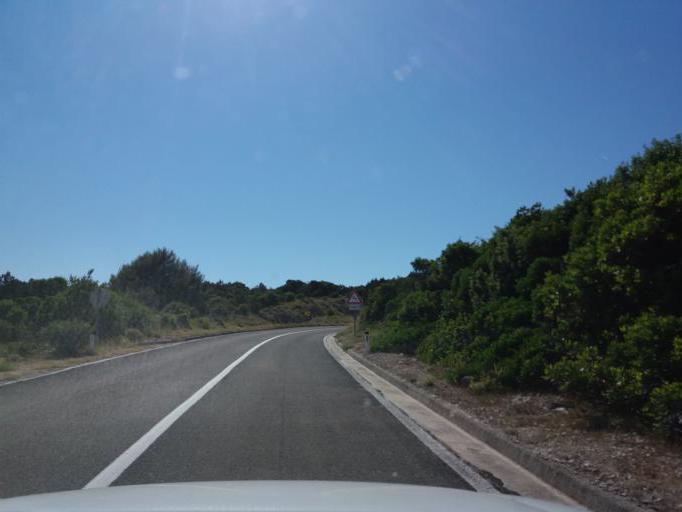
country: HR
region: Zadarska
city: Ugljan
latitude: 44.0865
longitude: 14.9637
